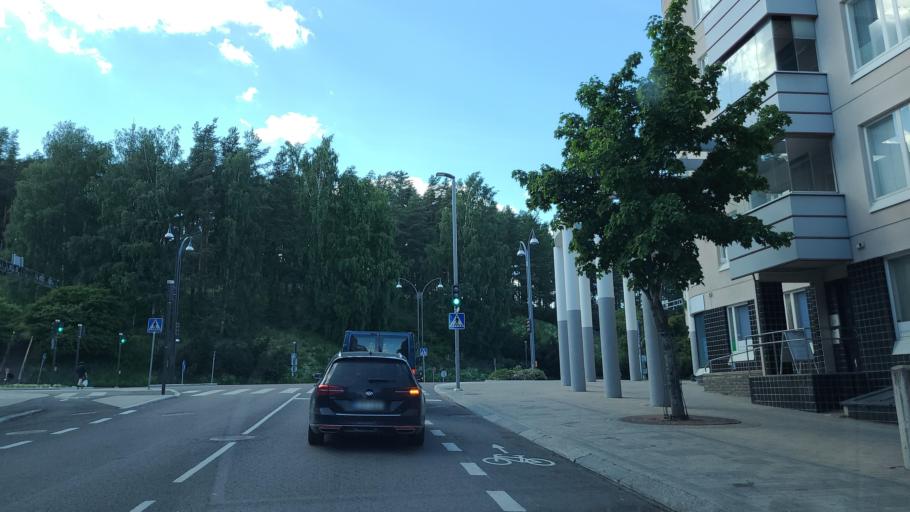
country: FI
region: Central Finland
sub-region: Jyvaeskylae
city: Jyvaeskylae
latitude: 62.2423
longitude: 25.7435
